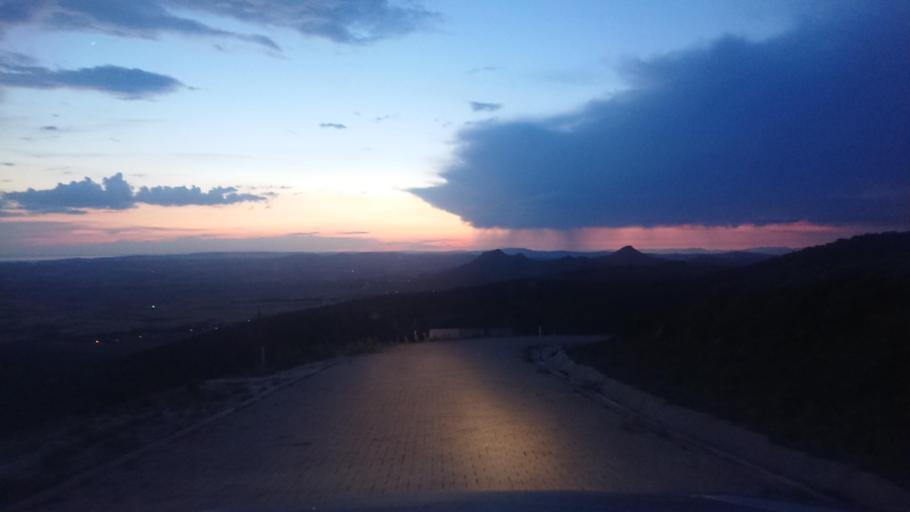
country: TR
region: Aksaray
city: Ortakoy
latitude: 38.6405
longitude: 34.0251
